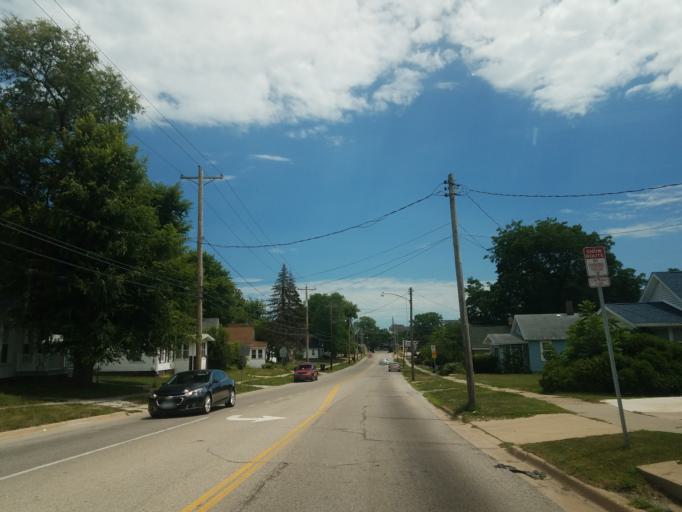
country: US
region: Illinois
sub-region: McLean County
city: Bloomington
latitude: 40.4827
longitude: -89.0113
